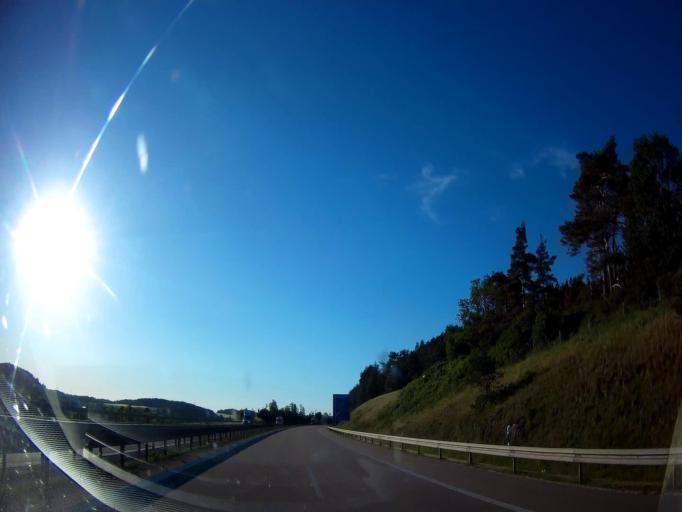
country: DE
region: Bavaria
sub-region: Upper Palatinate
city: Velburg
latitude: 49.2265
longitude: 11.6421
